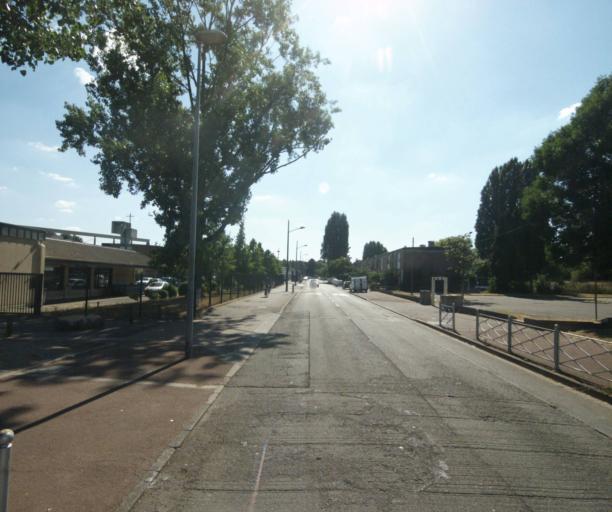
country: FR
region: Nord-Pas-de-Calais
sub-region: Departement du Nord
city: Neuville-en-Ferrain
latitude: 50.7402
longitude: 3.1810
